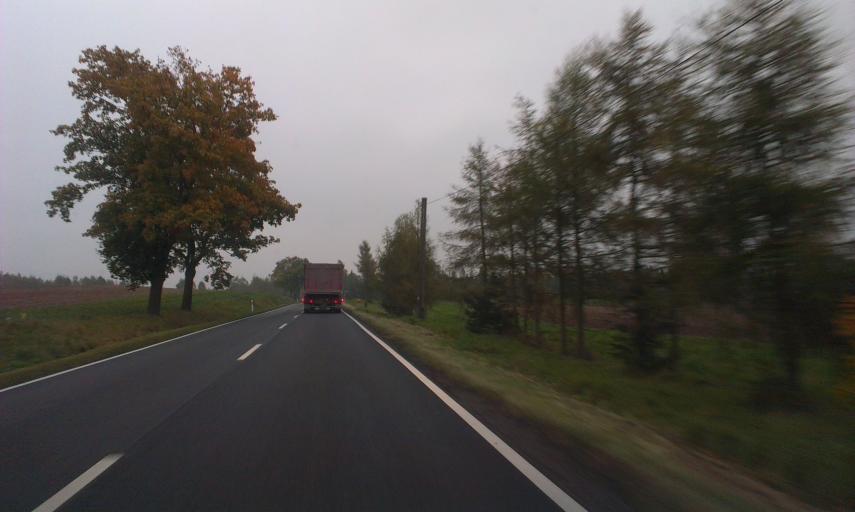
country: PL
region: Kujawsko-Pomorskie
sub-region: Powiat sepolenski
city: Sosno
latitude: 53.4383
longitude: 17.6203
